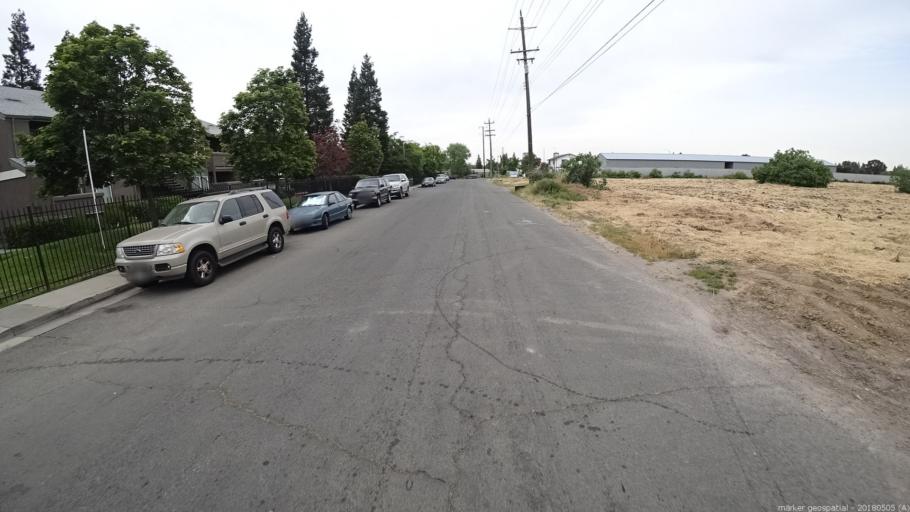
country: US
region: California
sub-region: Sacramento County
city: Rio Linda
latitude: 38.6429
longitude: -121.4523
